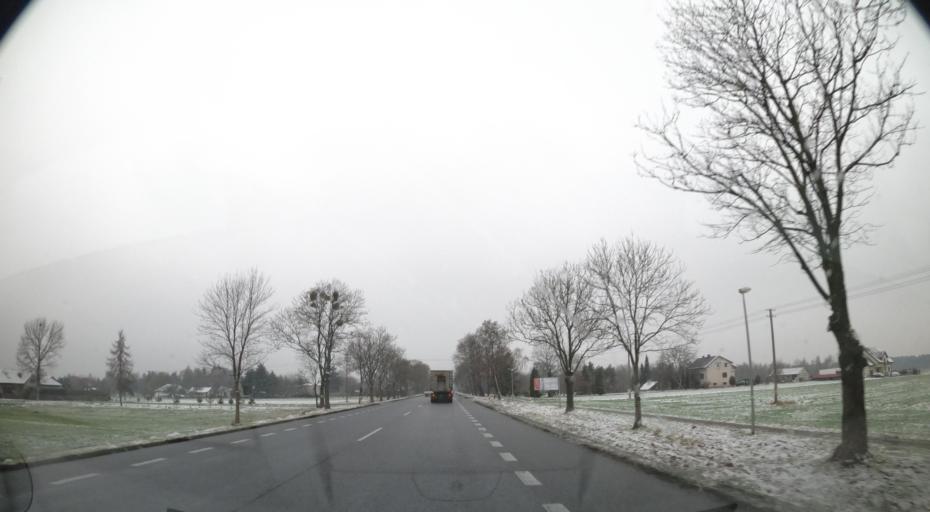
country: PL
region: Masovian Voivodeship
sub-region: Powiat sochaczewski
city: Teresin
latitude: 52.2176
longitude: 20.3688
